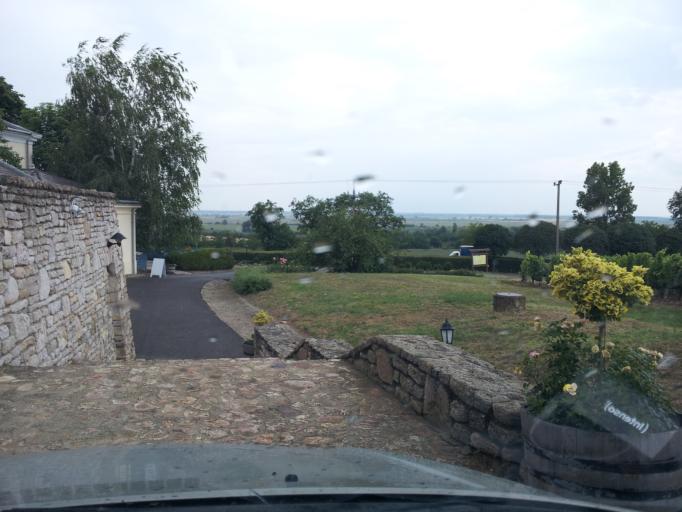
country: HU
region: Borsod-Abauj-Zemplen
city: Mad
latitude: 48.1658
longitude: 21.3030
